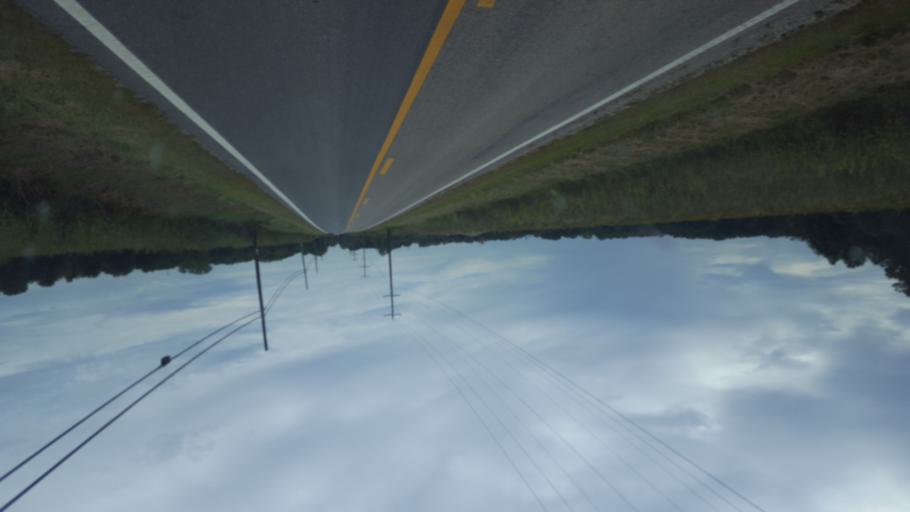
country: US
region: Ohio
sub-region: Delaware County
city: Sunbury
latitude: 40.2460
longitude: -82.8353
